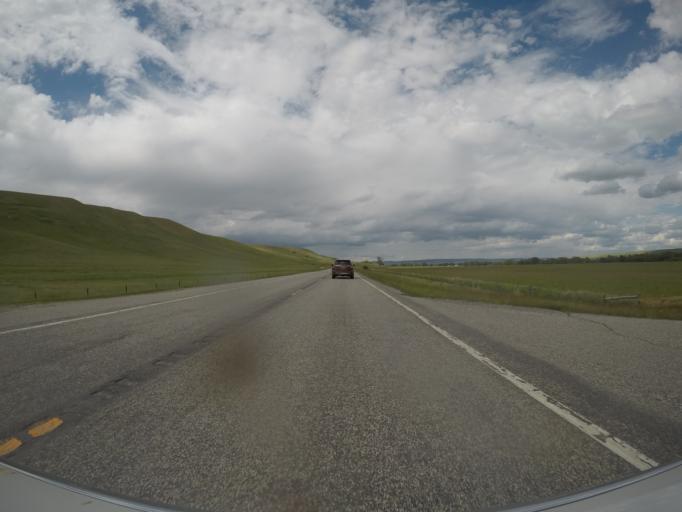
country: US
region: Montana
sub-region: Sweet Grass County
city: Big Timber
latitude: 45.7963
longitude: -109.9711
